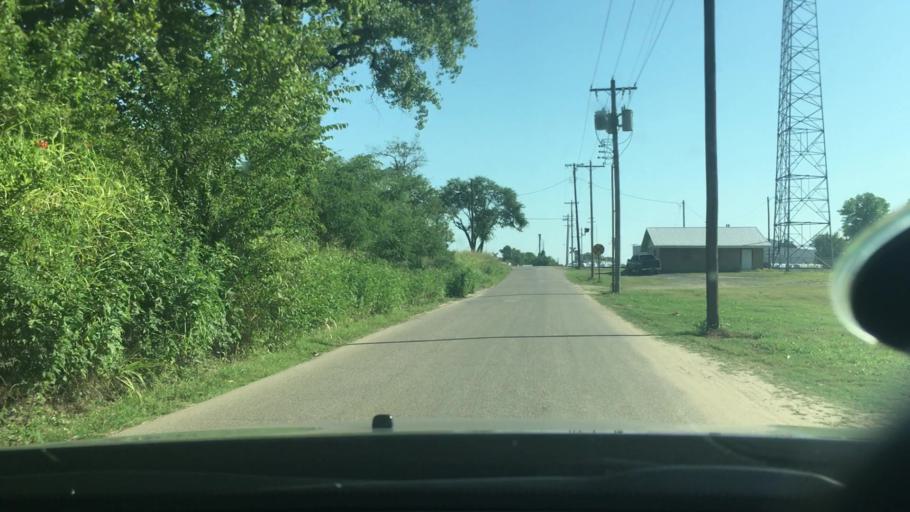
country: US
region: Oklahoma
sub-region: Bryan County
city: Durant
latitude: 33.9877
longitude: -96.3756
